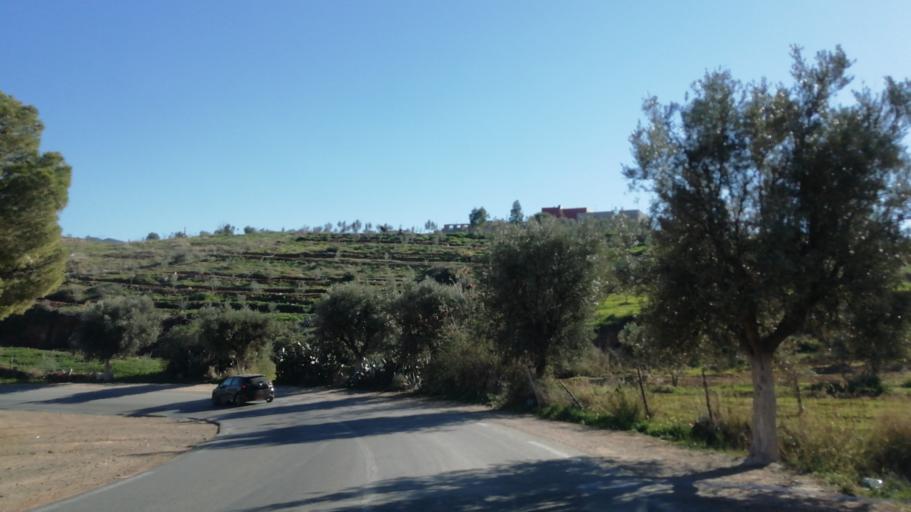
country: DZ
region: Tlemcen
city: Beni Mester
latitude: 34.8289
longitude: -1.5095
